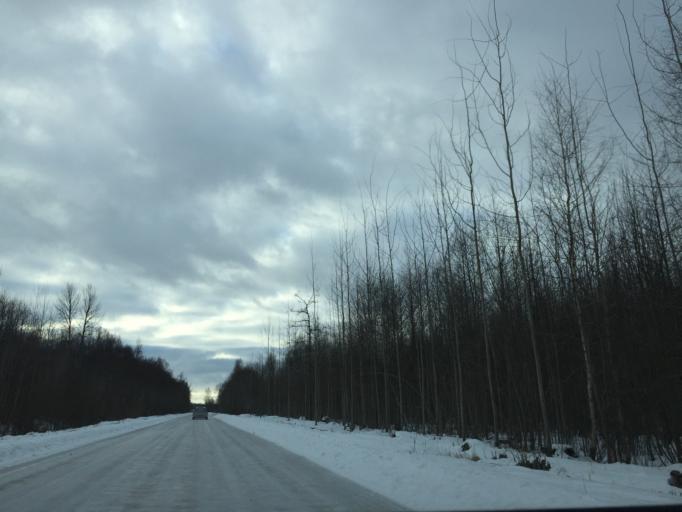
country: LV
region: Lielvarde
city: Lielvarde
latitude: 56.5961
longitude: 24.7397
